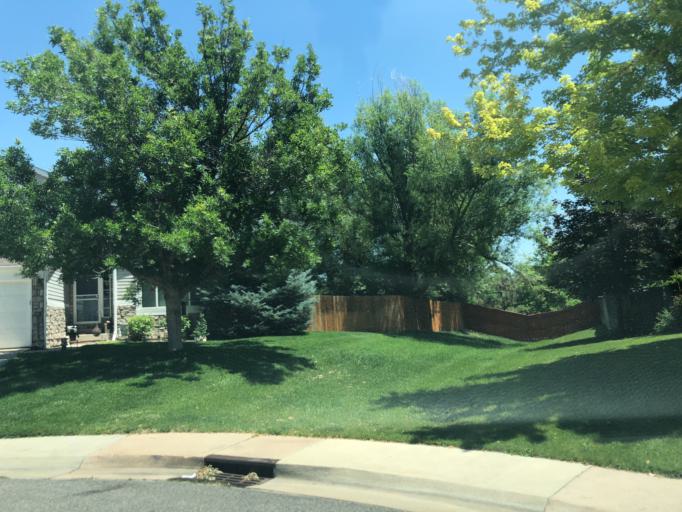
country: US
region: Colorado
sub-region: Arapahoe County
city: Dove Valley
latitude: 39.6205
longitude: -104.7548
